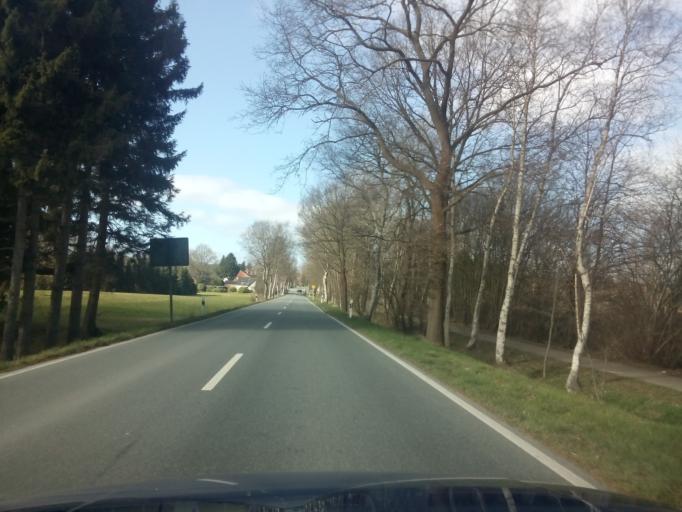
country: DE
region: Lower Saxony
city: Worpswede
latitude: 53.2173
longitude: 8.9467
